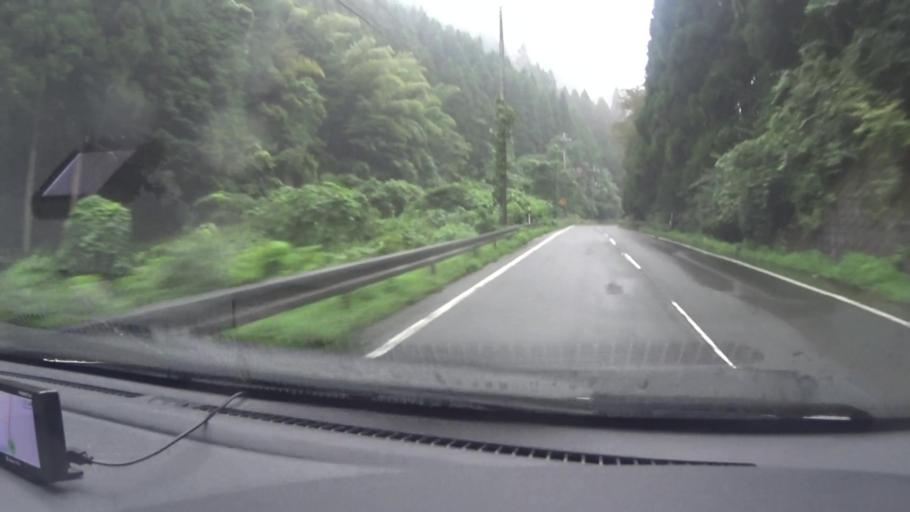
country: JP
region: Kyoto
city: Ayabe
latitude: 35.2398
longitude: 135.3029
